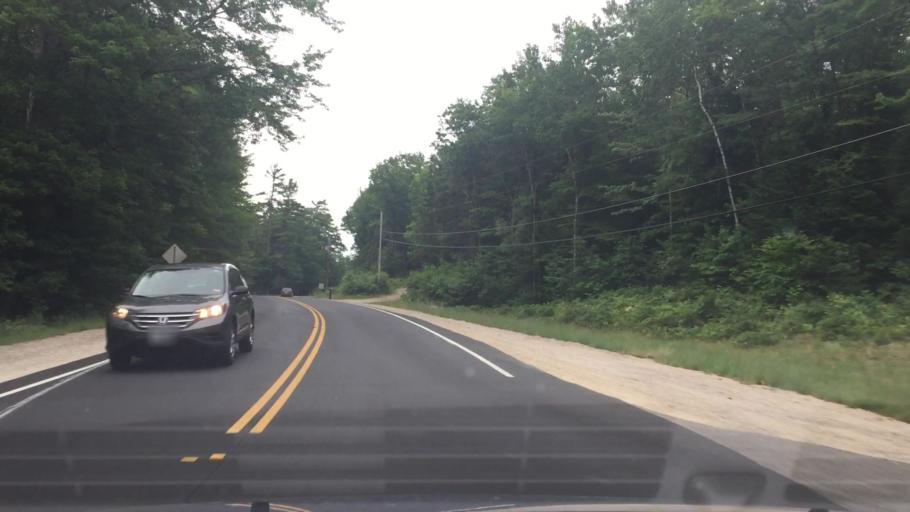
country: US
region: New Hampshire
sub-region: Carroll County
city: Freedom
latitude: 43.8065
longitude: -71.0634
